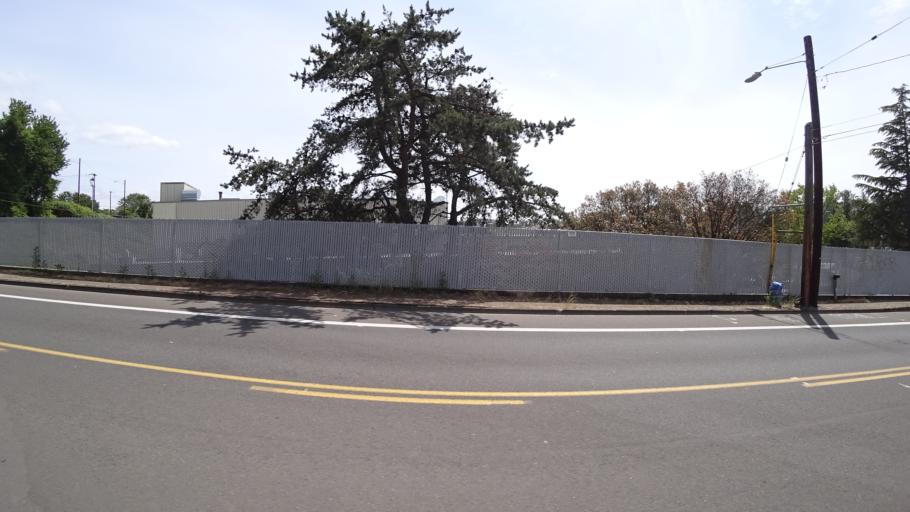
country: US
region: Oregon
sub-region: Clackamas County
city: Milwaukie
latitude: 45.4627
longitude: -122.6139
